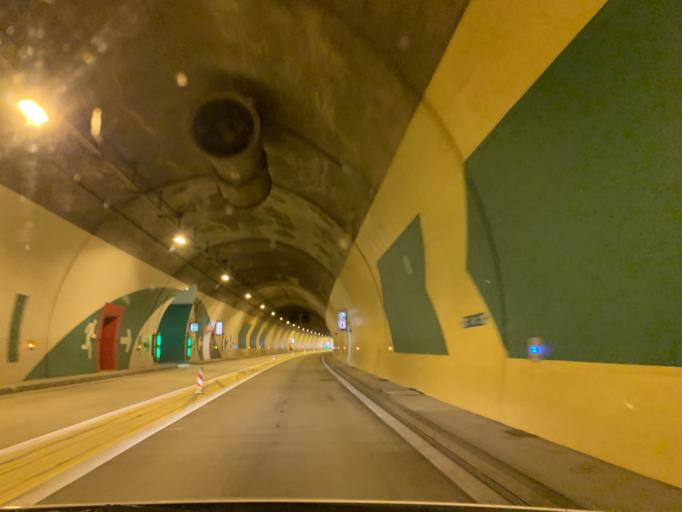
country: FR
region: Rhone-Alpes
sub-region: Departement de l'Isere
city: La Motte-Saint-Martin
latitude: 44.9373
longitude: 5.6440
